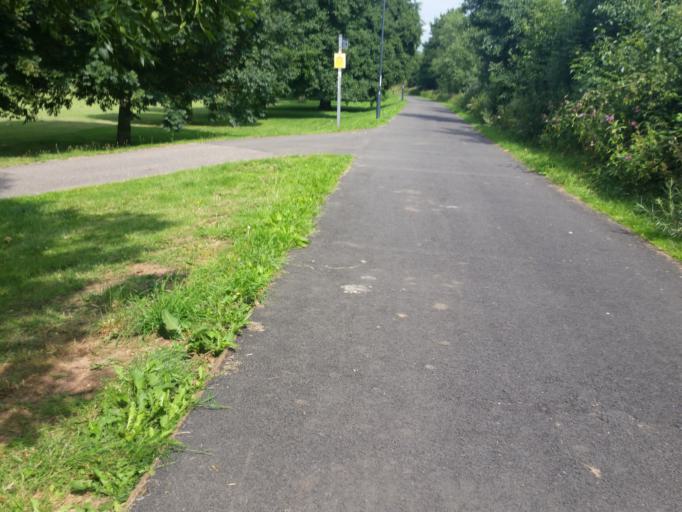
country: GB
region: England
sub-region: Derby
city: Derby
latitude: 52.9064
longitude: -1.4358
